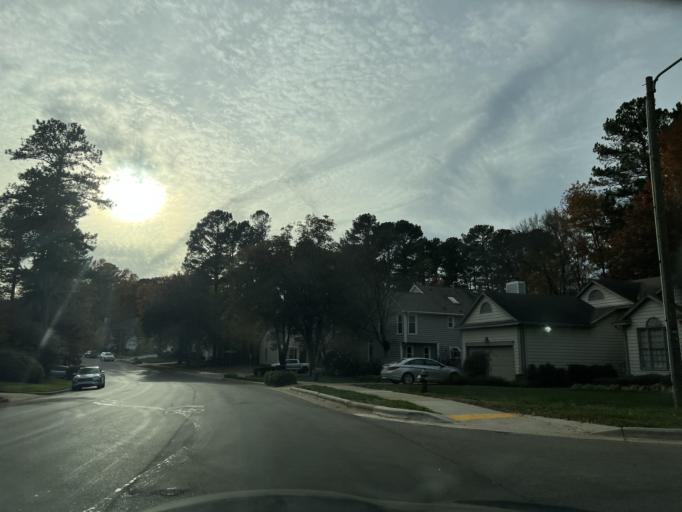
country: US
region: North Carolina
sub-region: Wake County
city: Wake Forest
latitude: 35.9019
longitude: -78.5854
